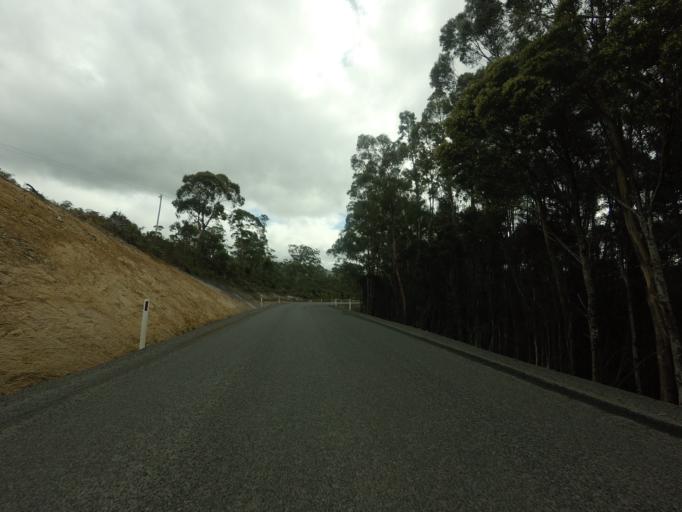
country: AU
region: Tasmania
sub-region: Huon Valley
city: Geeveston
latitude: -43.4243
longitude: 146.9051
